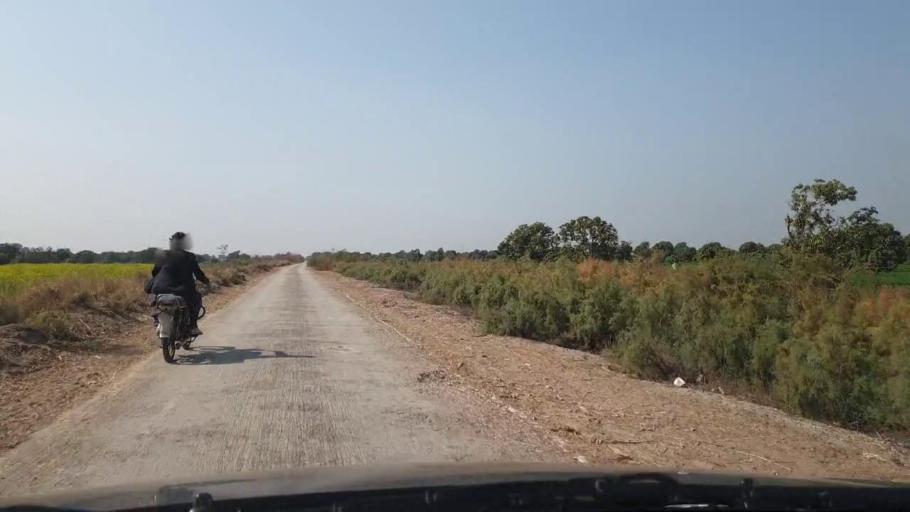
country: PK
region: Sindh
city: Jhol
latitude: 25.8923
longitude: 68.9273
